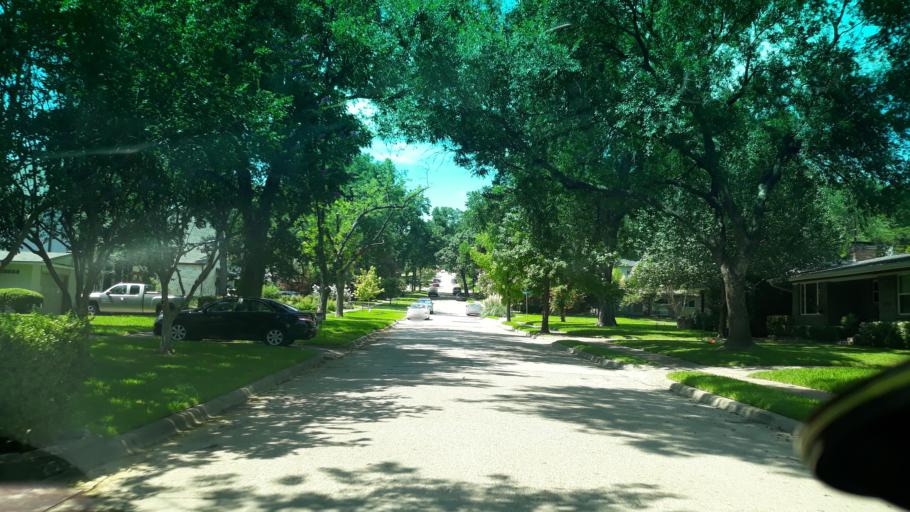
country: US
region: Texas
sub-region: Dallas County
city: Highland Park
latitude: 32.8162
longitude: -96.7326
